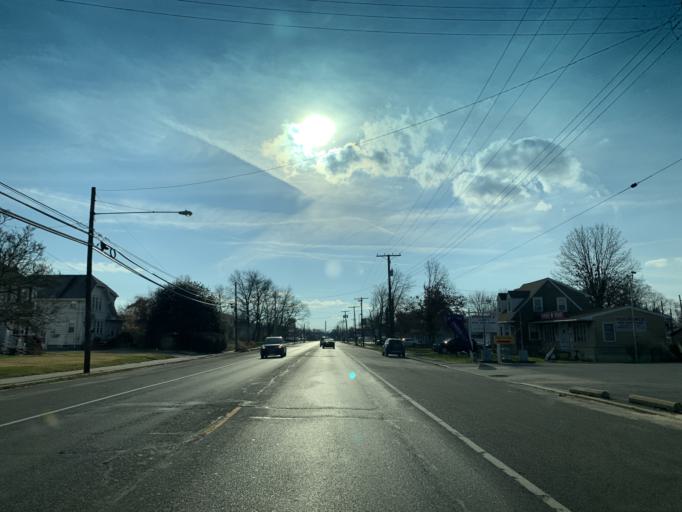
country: US
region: New Jersey
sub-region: Salem County
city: Penns Grove
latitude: 39.7283
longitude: -75.4626
